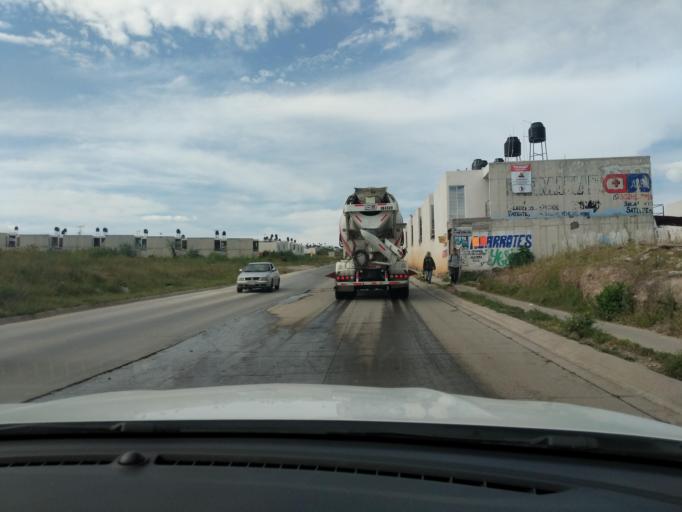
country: MX
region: Jalisco
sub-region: El Salto
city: Galaxia Bonito Jalisco
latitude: 20.5104
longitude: -103.2085
